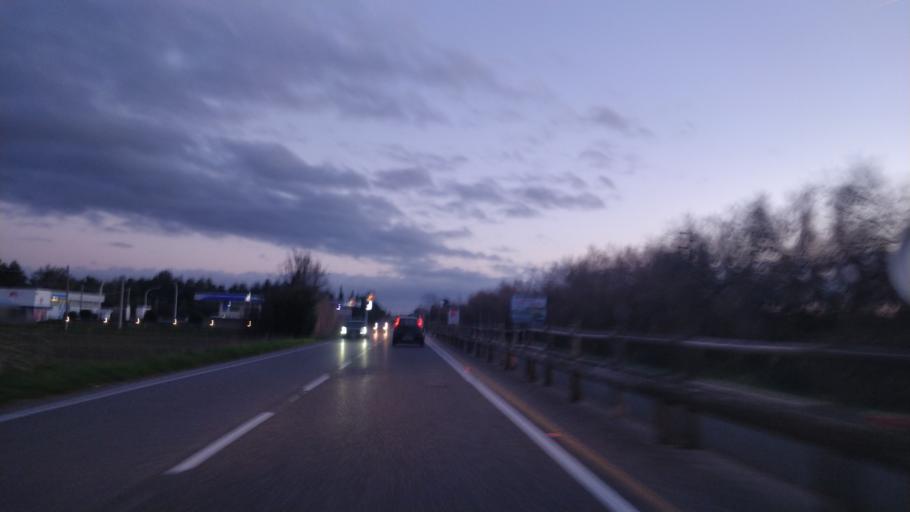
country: IT
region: Tuscany
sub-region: Provincia di Livorno
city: Vada
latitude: 43.3646
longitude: 10.4520
